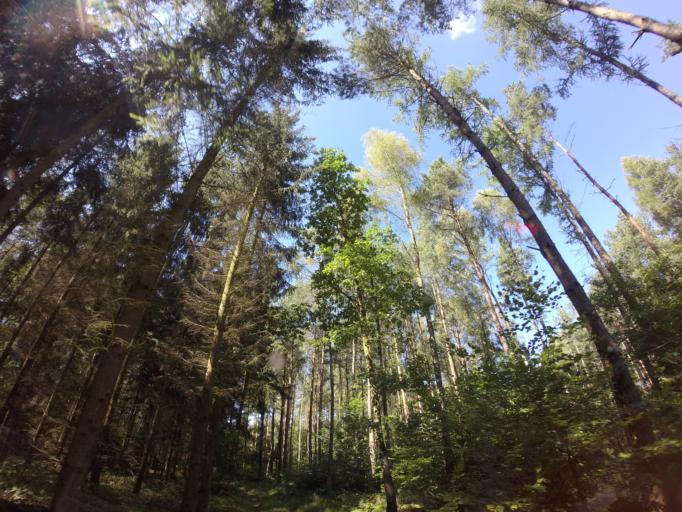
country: PL
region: West Pomeranian Voivodeship
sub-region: Powiat choszczenski
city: Recz
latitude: 53.2293
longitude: 15.6424
